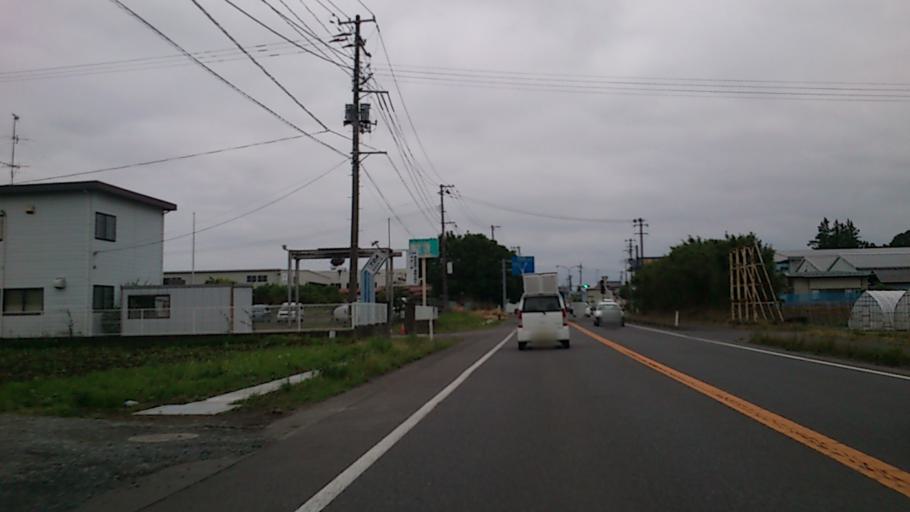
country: JP
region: Fukushima
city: Sukagawa
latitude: 37.2177
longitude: 140.3283
